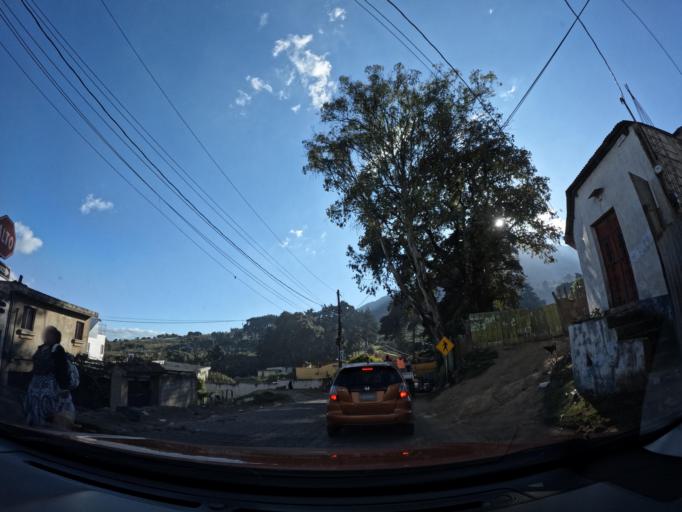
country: GT
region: Sacatepequez
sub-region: Municipio de Santa Maria de Jesus
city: Santa Maria de Jesus
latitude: 14.4893
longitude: -90.7087
